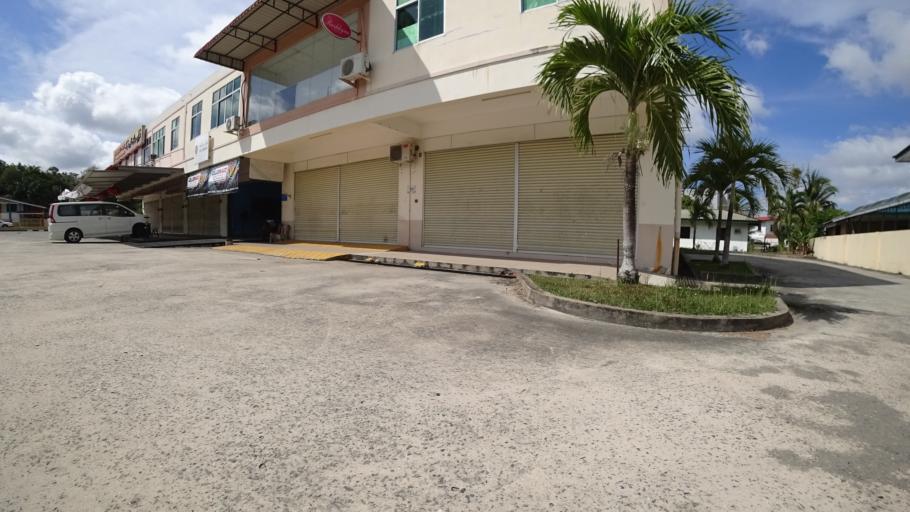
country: BN
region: Brunei and Muara
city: Bandar Seri Begawan
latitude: 4.8931
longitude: 114.8482
